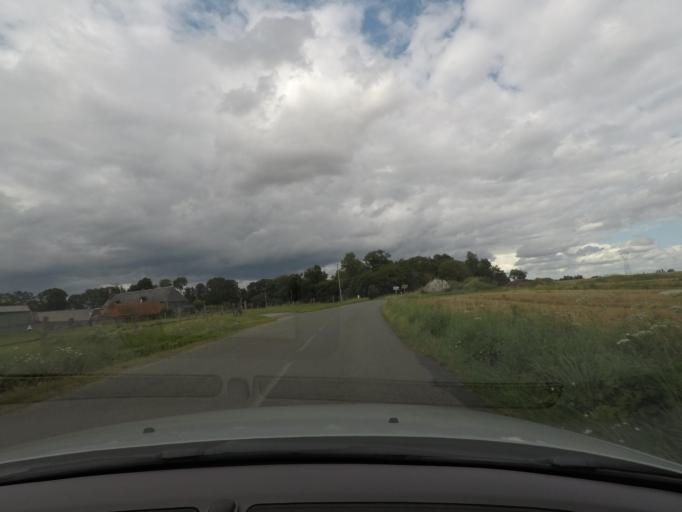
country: FR
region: Haute-Normandie
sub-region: Departement de l'Eure
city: Les Andelys
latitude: 49.2816
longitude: 1.3587
